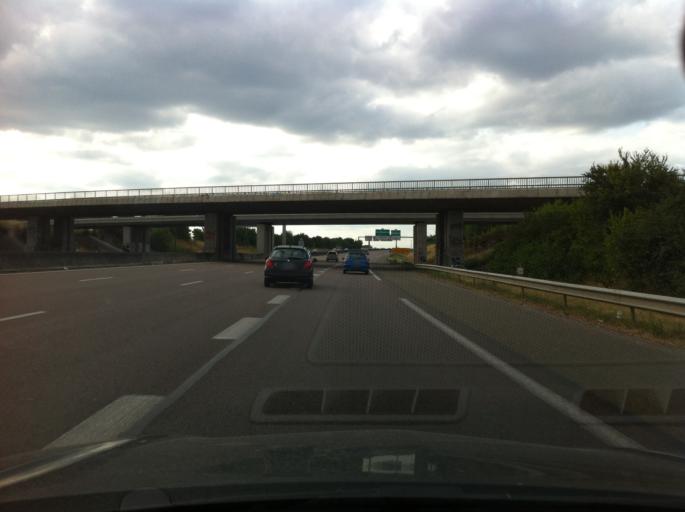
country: FR
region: Ile-de-France
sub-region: Departement de Seine-et-Marne
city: Lieusaint
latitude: 48.6230
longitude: 2.5436
